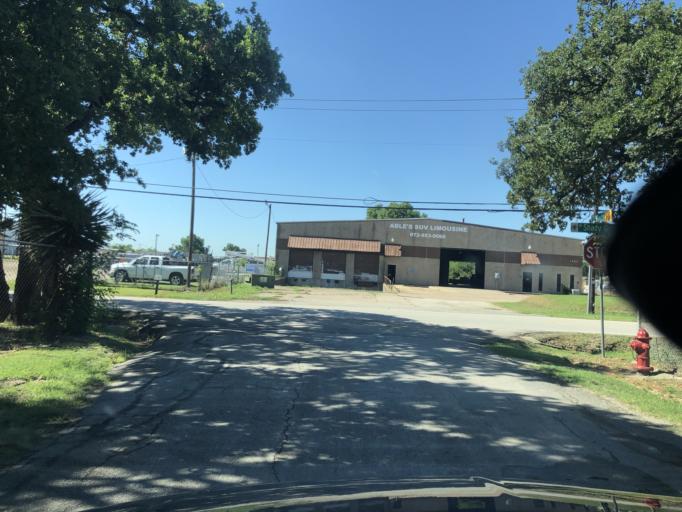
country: US
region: Texas
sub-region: Dallas County
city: Grand Prairie
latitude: 32.8037
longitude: -97.0218
